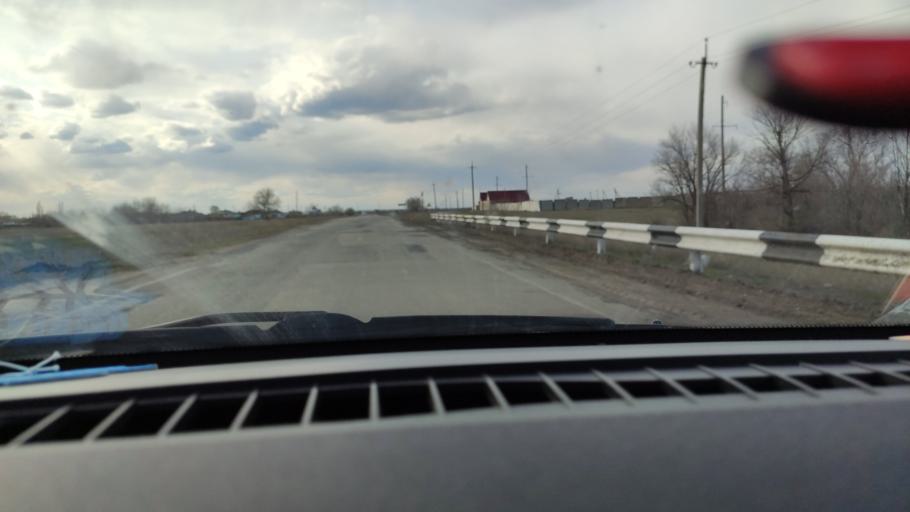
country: RU
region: Saratov
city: Rovnoye
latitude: 51.0604
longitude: 46.0230
